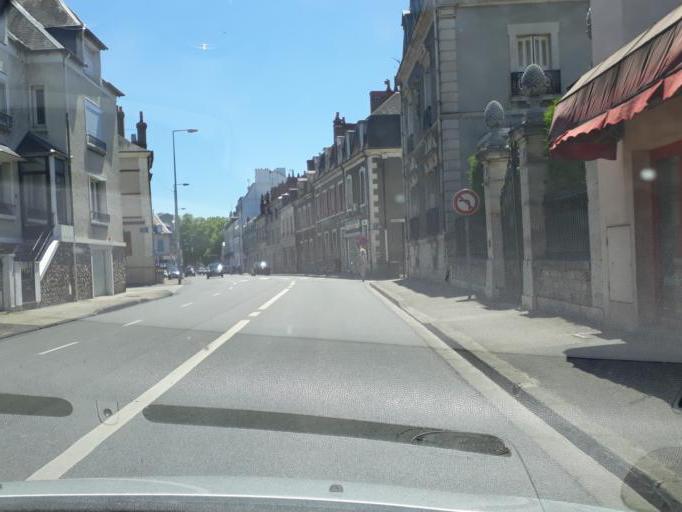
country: FR
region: Centre
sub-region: Departement du Cher
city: Bourges
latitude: 47.0860
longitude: 2.3884
